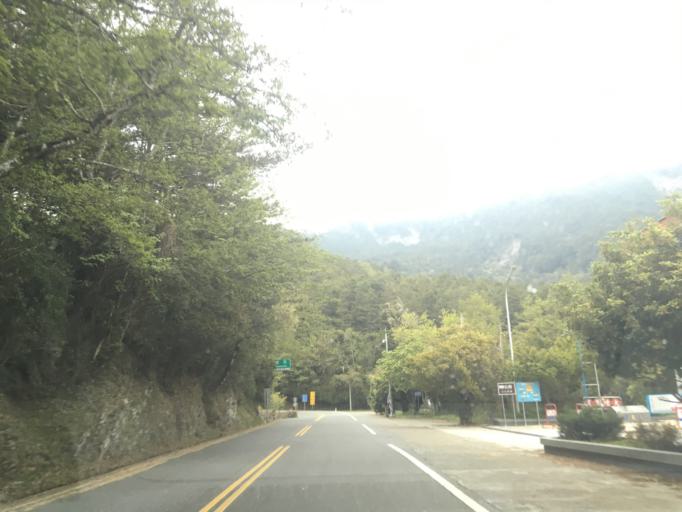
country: TW
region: Taiwan
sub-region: Hualien
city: Hualian
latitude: 24.1848
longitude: 121.3421
